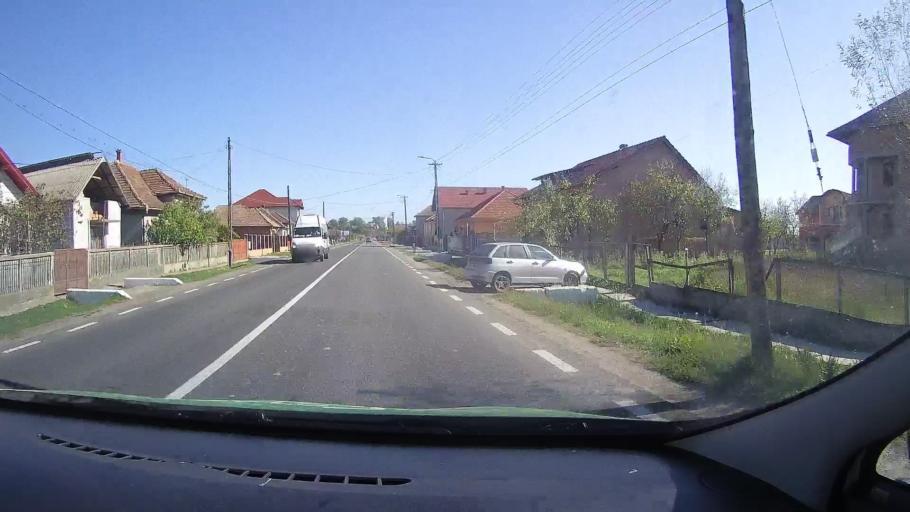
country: RO
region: Satu Mare
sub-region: Oras Ardud
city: Ardud
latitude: 47.6531
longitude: 22.8877
